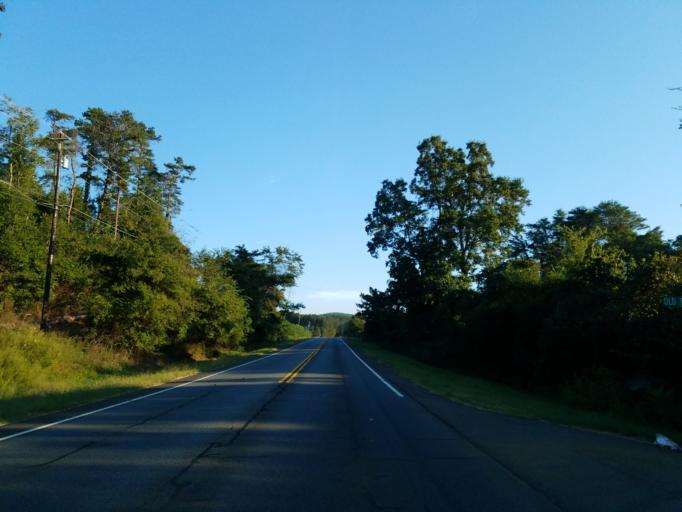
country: US
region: Georgia
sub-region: Bartow County
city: Rydal
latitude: 34.3402
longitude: -84.7172
